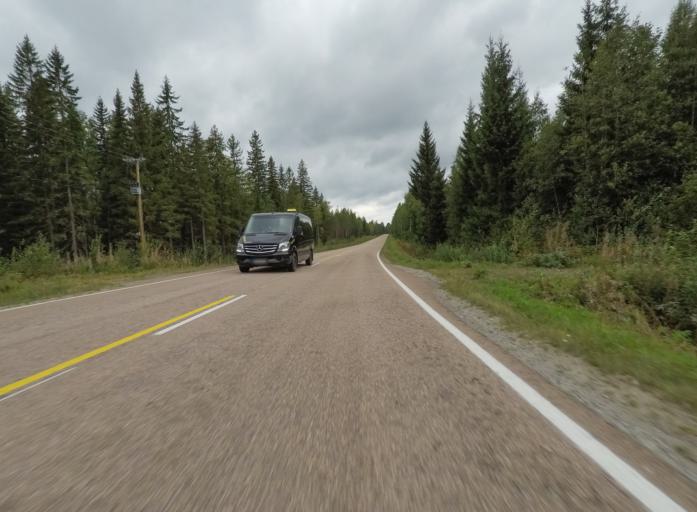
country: FI
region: Central Finland
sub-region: Jyvaeskylae
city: Hankasalmi
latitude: 62.3585
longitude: 26.5562
